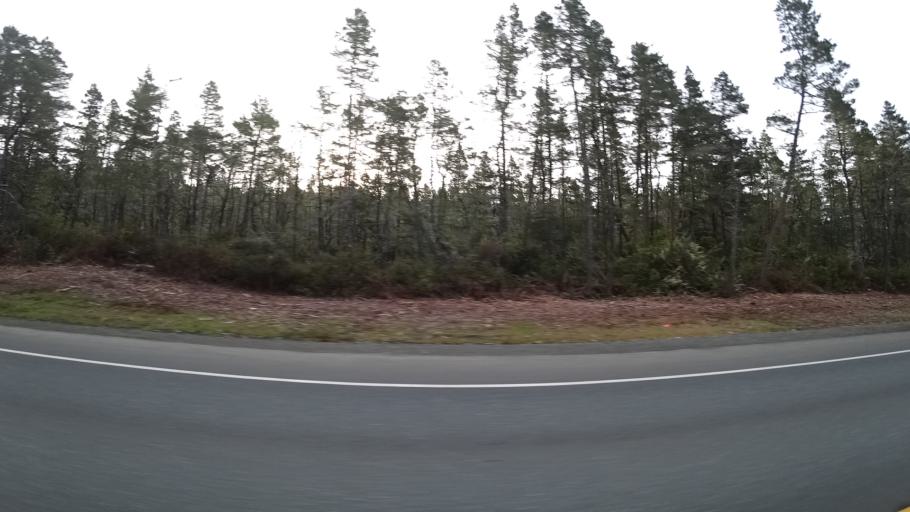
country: US
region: Oregon
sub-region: Coos County
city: Lakeside
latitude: 43.5841
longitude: -124.1846
